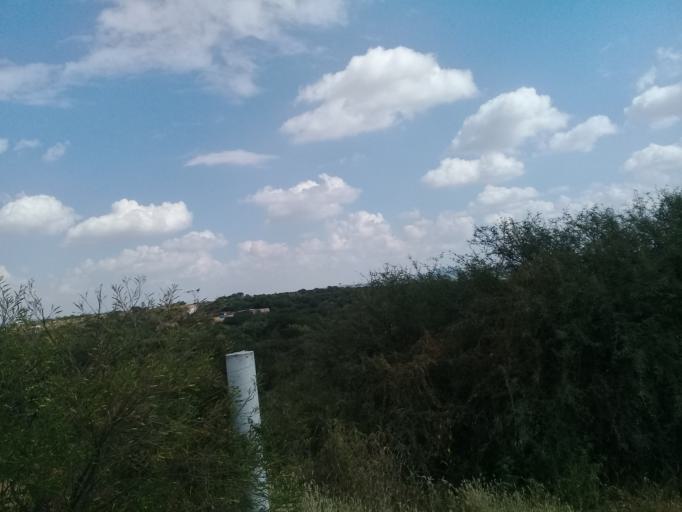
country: MX
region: Aguascalientes
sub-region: Aguascalientes
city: Penuelas (El Cienegal)
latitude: 21.7737
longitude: -102.3277
